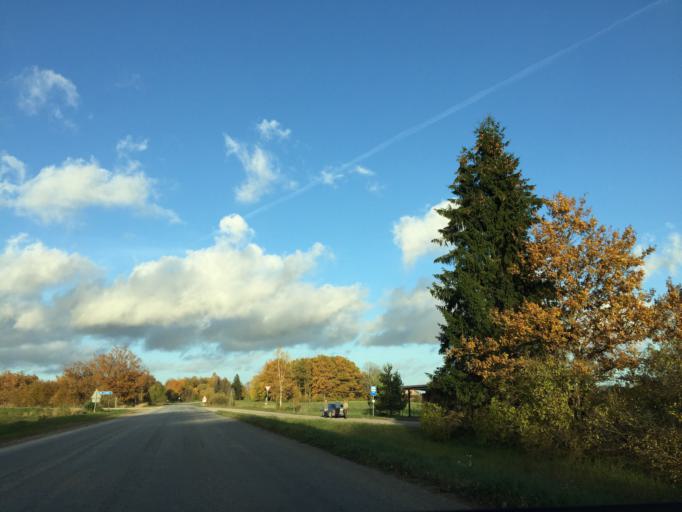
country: LV
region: Ogre
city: Jumprava
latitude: 56.7956
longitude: 25.0433
